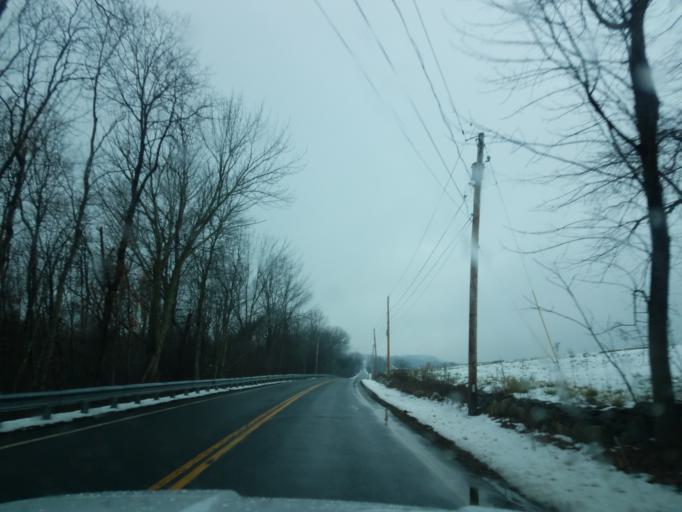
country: US
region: Massachusetts
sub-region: Worcester County
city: Southbridge
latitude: 42.0303
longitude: -72.0110
